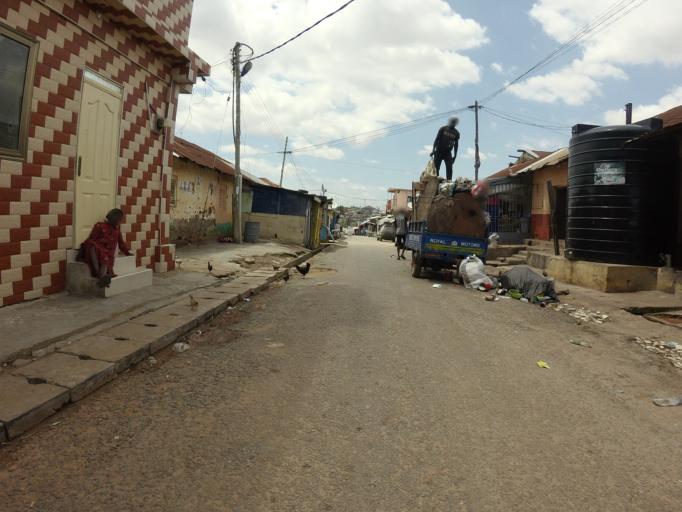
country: GH
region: Greater Accra
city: Accra
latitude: 5.5814
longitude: -0.2013
